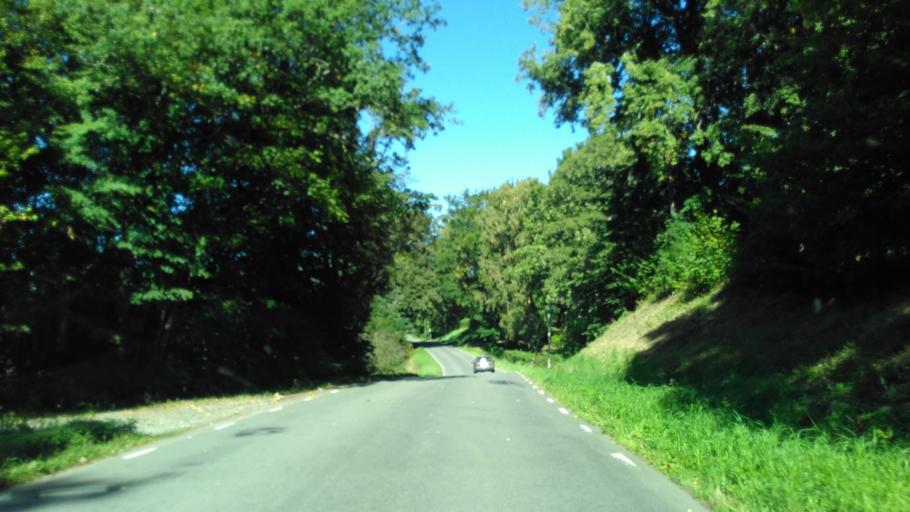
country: SE
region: Vaestra Goetaland
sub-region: Skara Kommun
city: Axvall
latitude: 58.4490
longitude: 13.6649
